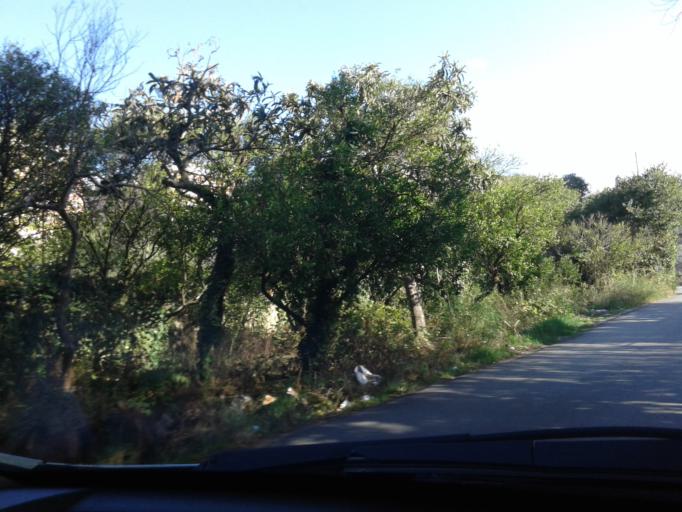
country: IT
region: Sicily
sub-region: Palermo
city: Monreale
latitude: 38.1010
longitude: 13.3163
